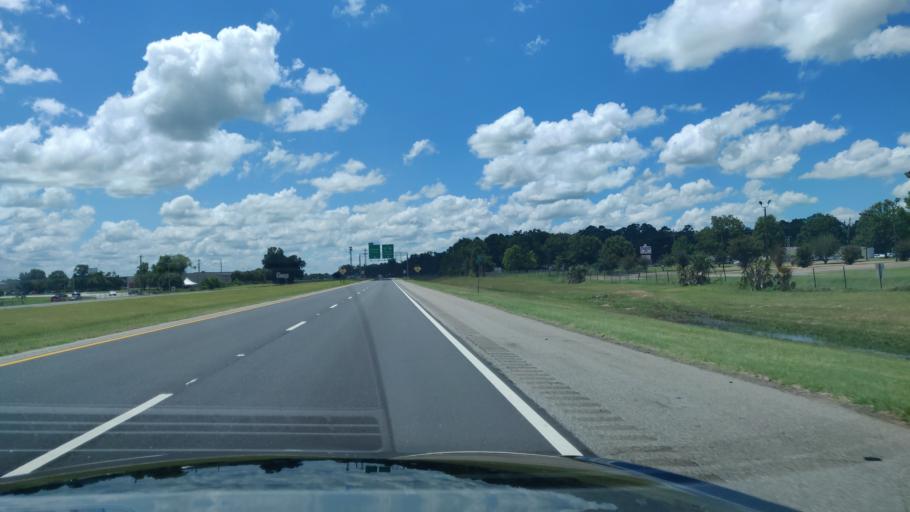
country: US
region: Georgia
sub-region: Dougherty County
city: Albany
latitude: 31.6211
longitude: -84.2163
